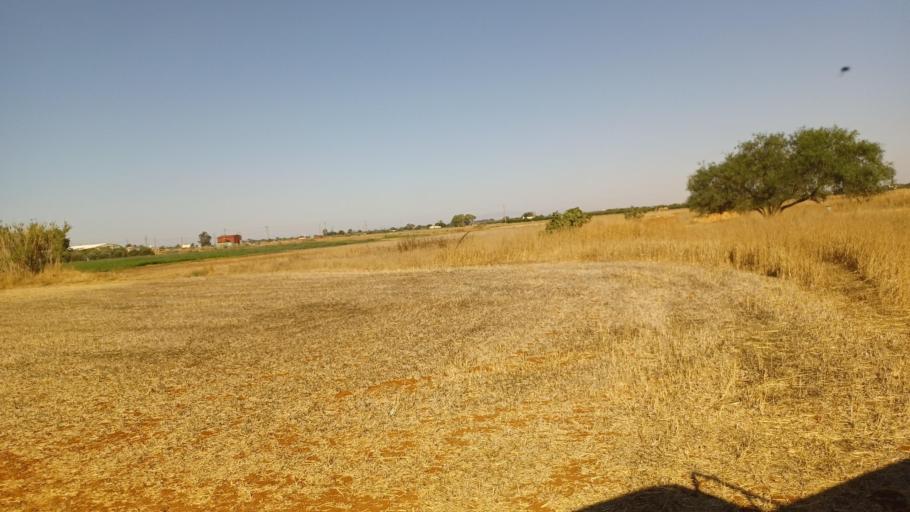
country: CY
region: Ammochostos
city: Avgorou
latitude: 35.0145
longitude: 33.8469
